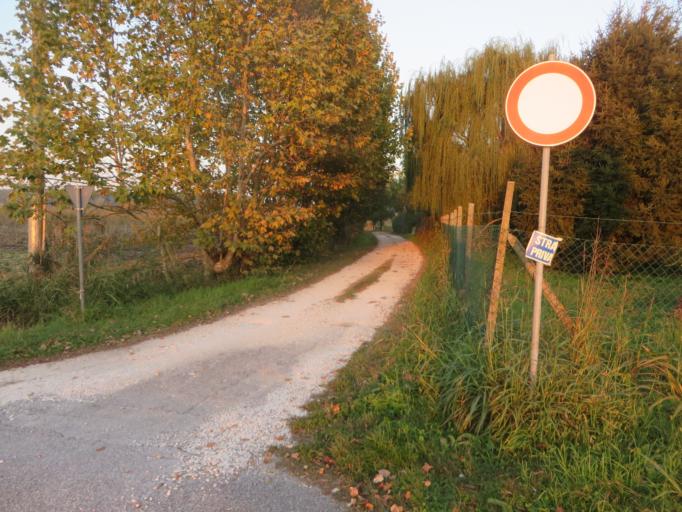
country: IT
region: Veneto
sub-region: Provincia di Verona
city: San Pietro di Morubio
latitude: 45.2273
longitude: 11.2443
